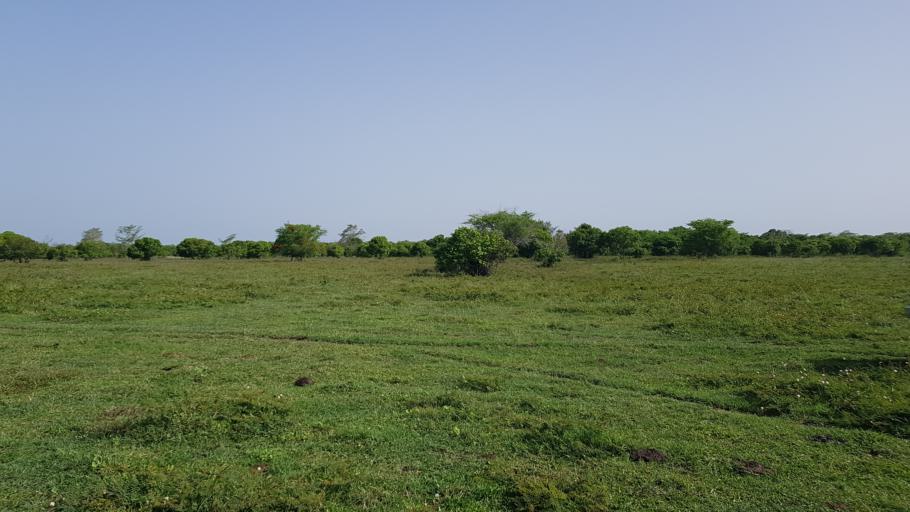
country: MX
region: Chiapas
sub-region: Catazaja
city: Catazaja
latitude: 17.8732
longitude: -92.1182
